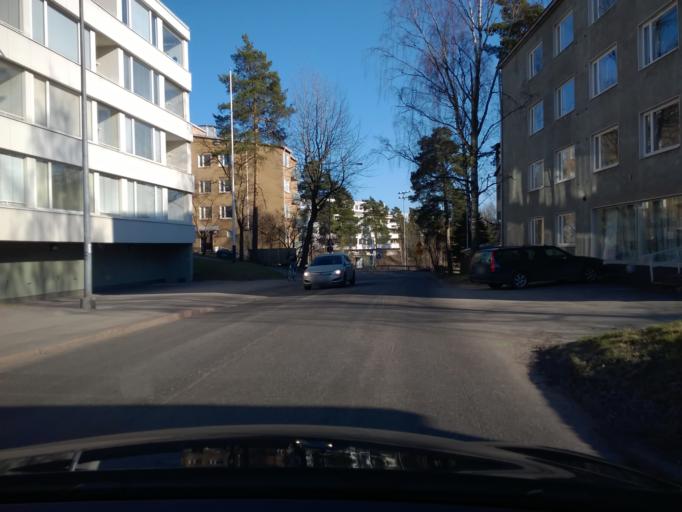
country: FI
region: Uusimaa
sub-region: Helsinki
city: Teekkarikylae
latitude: 60.2167
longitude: 24.8924
